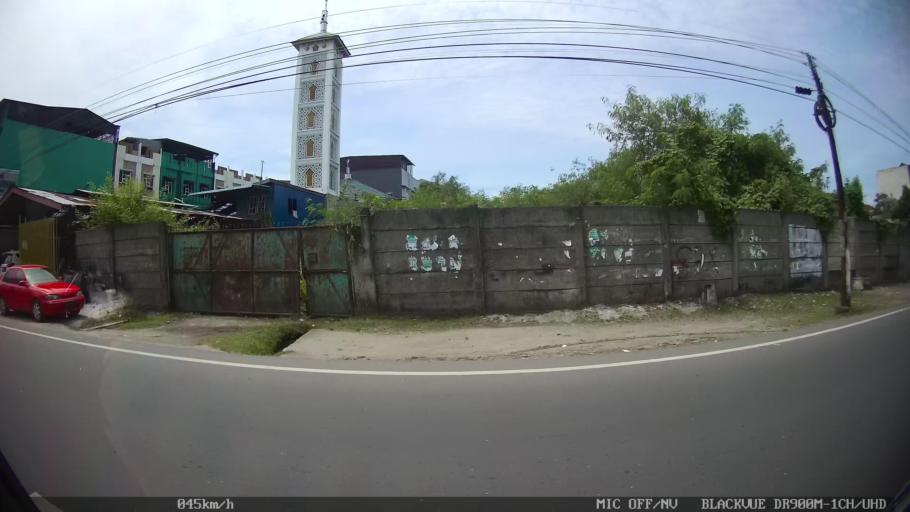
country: ID
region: North Sumatra
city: Sunggal
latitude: 3.5765
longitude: 98.6191
